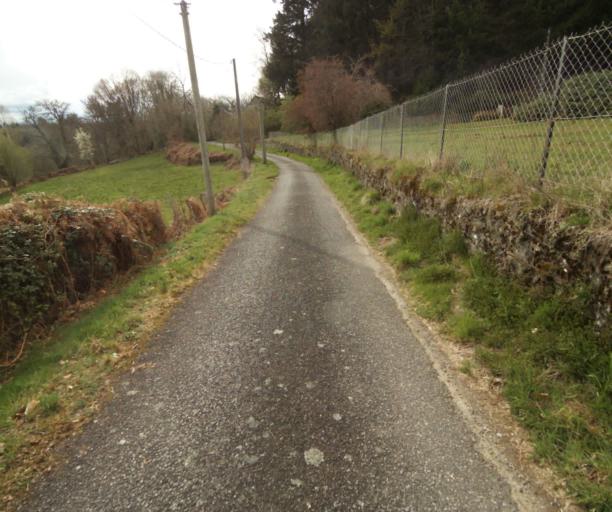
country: FR
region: Limousin
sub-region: Departement de la Correze
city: Argentat
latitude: 45.1989
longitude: 1.9613
